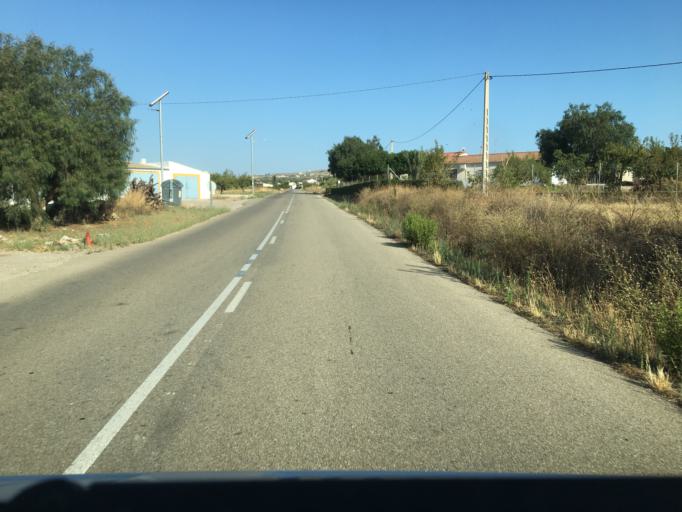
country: ES
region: Andalusia
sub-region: Provincia de Almeria
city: Huercal-Overa
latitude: 37.4673
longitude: -1.8874
